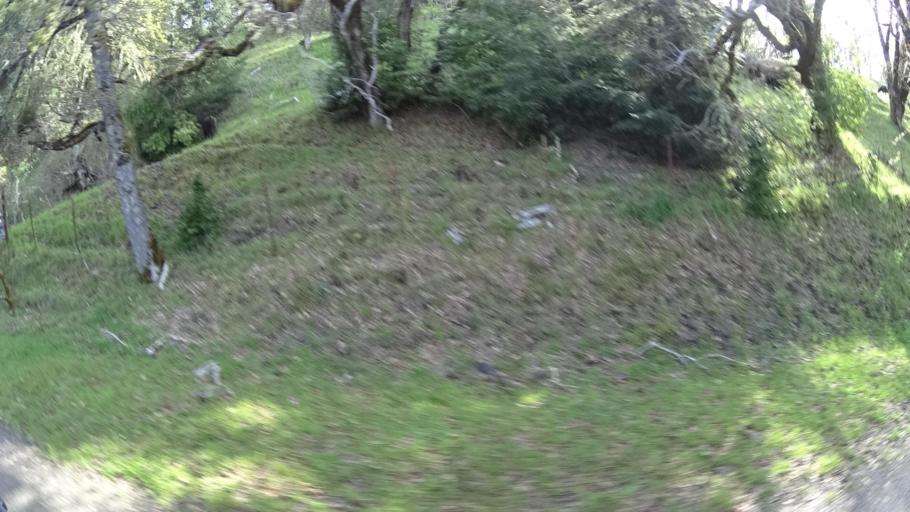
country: US
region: California
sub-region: Humboldt County
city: Hydesville
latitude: 40.6423
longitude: -123.9051
